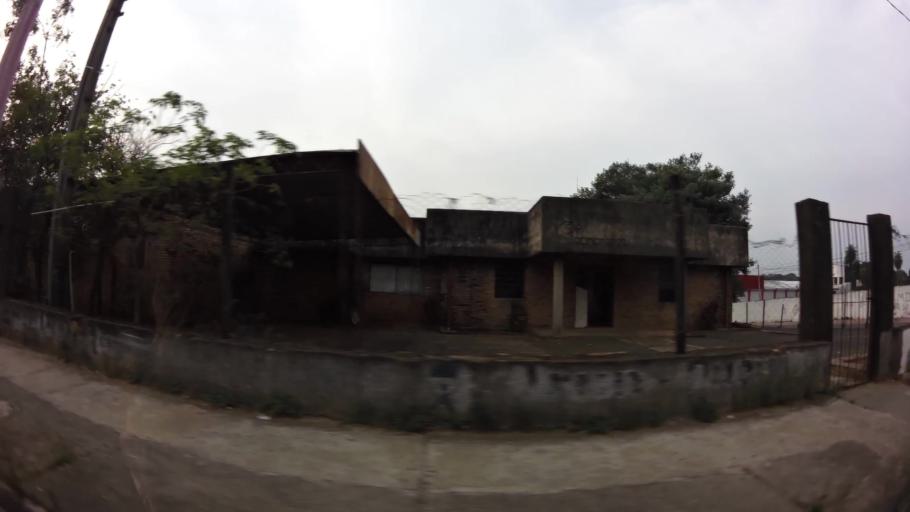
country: PY
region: Central
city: Lambare
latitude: -25.3432
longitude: -57.6104
